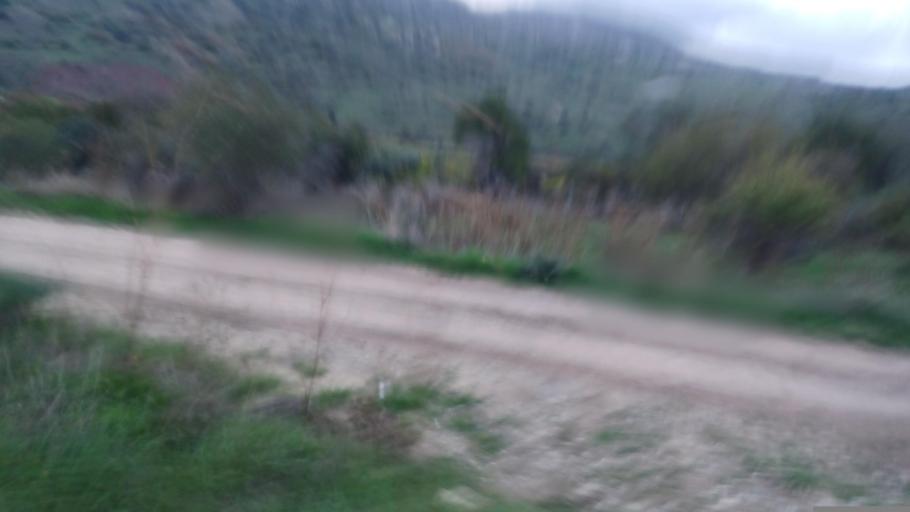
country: CY
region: Pafos
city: Mesogi
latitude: 34.7905
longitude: 32.5295
